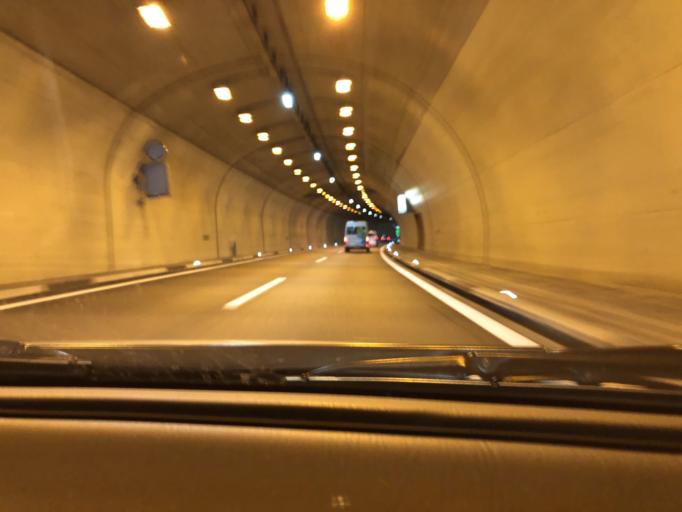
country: CH
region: Bern
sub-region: Biel/Bienne District
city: Pieterlen
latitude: 47.1692
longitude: 7.3300
